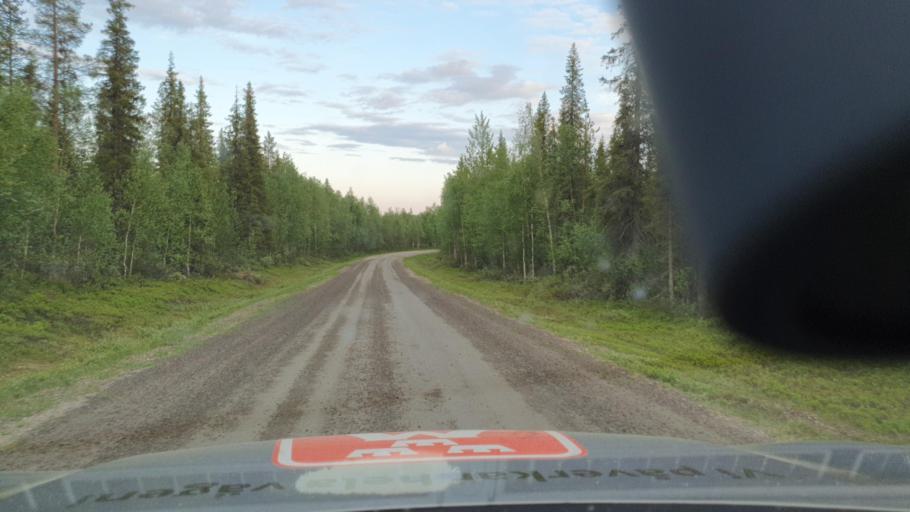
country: SE
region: Norrbotten
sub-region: Bodens Kommun
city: Boden
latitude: 66.6164
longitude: 21.3520
